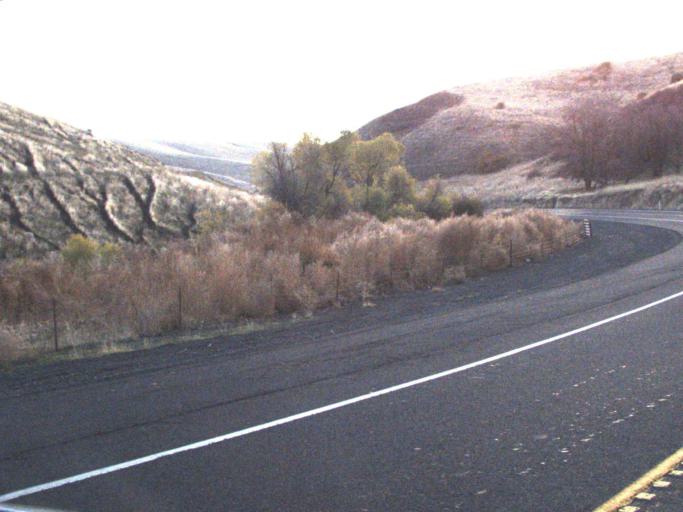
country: US
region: Washington
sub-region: Garfield County
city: Pomeroy
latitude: 46.6733
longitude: -117.8152
